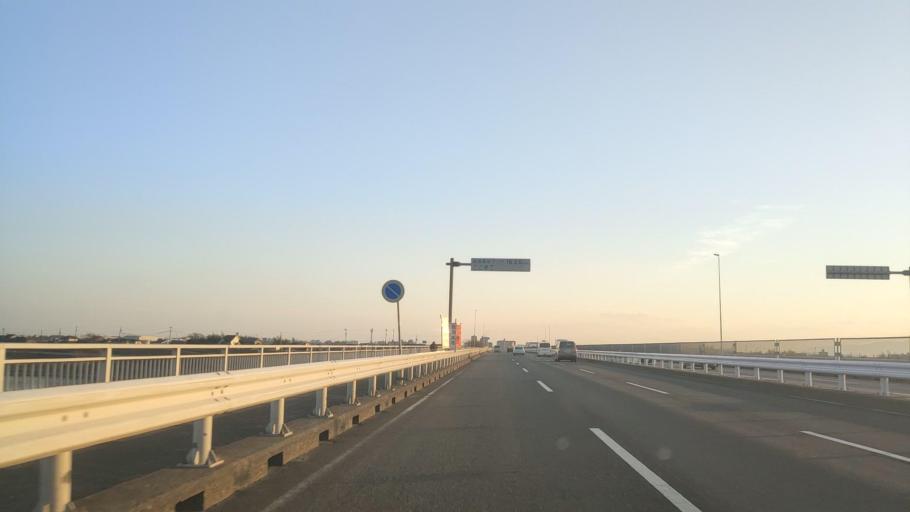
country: JP
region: Gifu
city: Kasamatsucho
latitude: 35.3700
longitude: 136.7837
